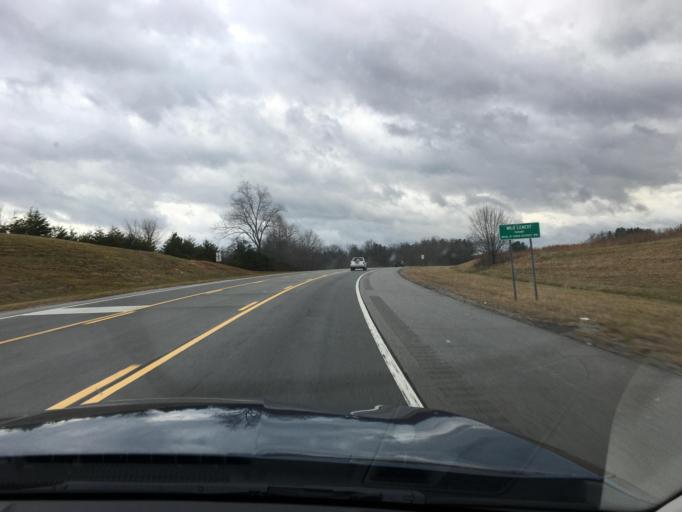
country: US
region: Tennessee
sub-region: Cumberland County
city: Crossville
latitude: 35.9546
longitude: -84.9846
